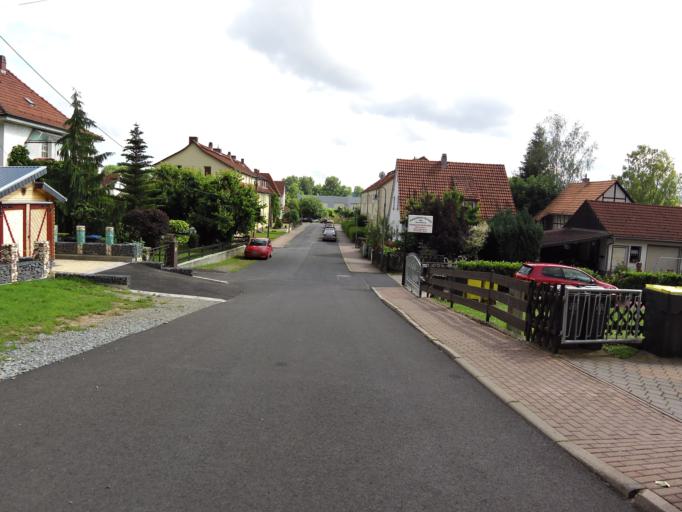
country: DE
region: Thuringia
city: Creuzburg
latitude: 51.0524
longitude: 10.2367
